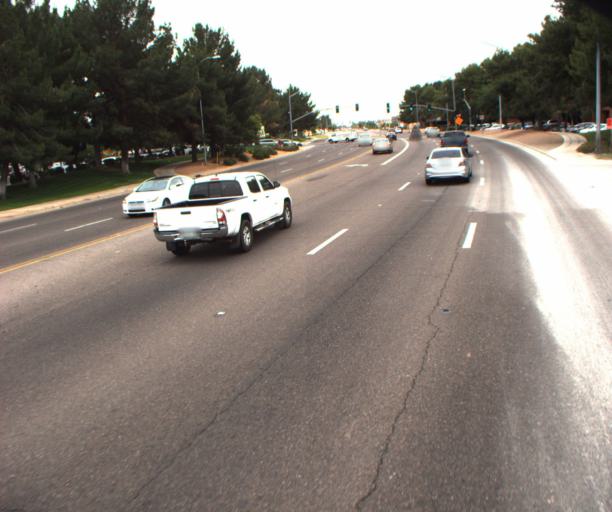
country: US
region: Arizona
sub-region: Maricopa County
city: San Carlos
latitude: 33.3769
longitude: -111.8423
